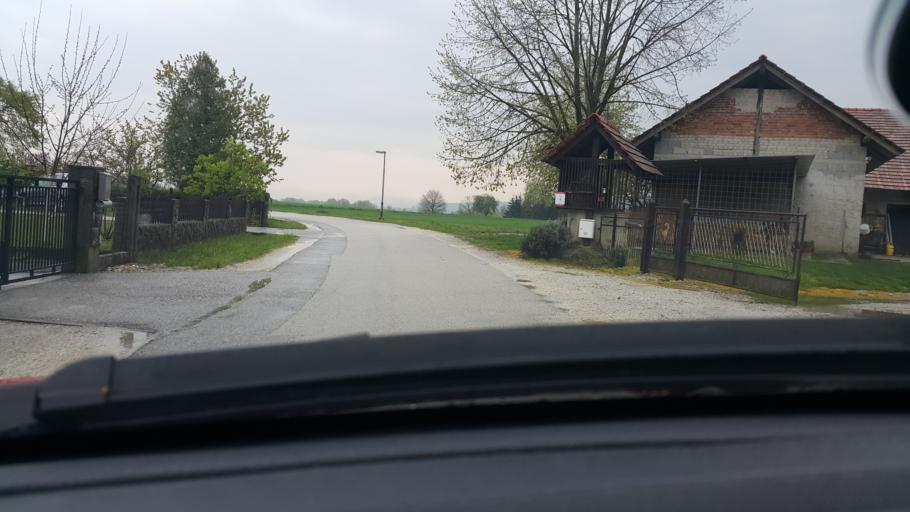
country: SI
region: Brezice
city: Brezice
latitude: 45.9121
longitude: 15.6213
